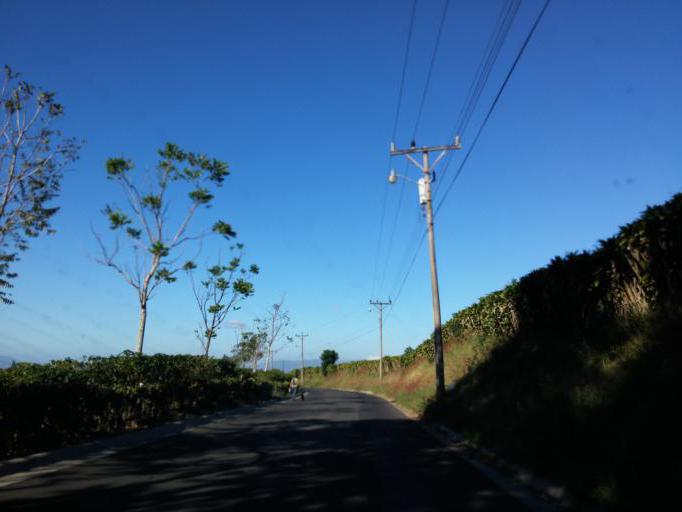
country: CR
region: Alajuela
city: Sabanilla
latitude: 10.0769
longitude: -84.1966
